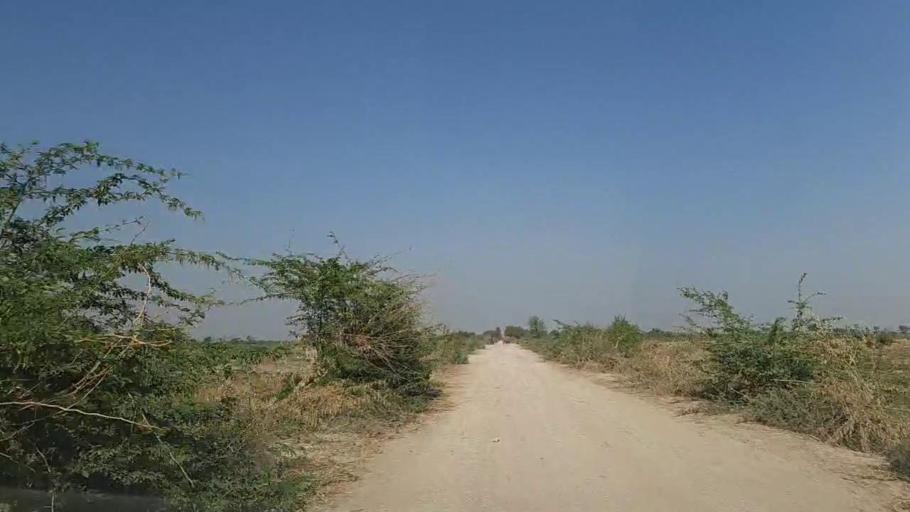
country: PK
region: Sindh
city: Samaro
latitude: 25.1912
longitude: 69.4041
